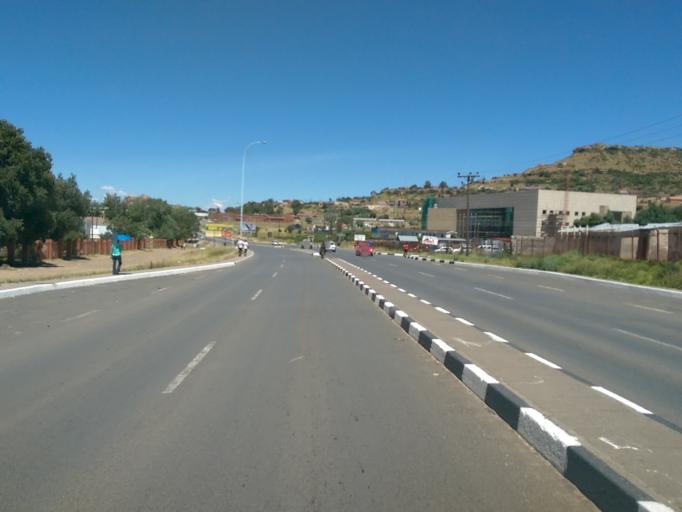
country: LS
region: Maseru
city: Maseru
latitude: -29.3212
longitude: 27.4974
